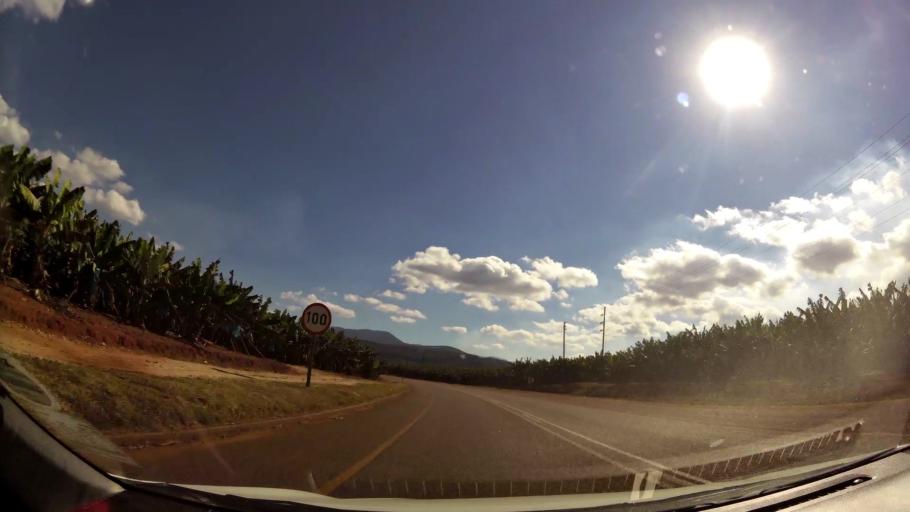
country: ZA
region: Limpopo
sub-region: Mopani District Municipality
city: Tzaneen
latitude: -23.8039
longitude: 30.1097
